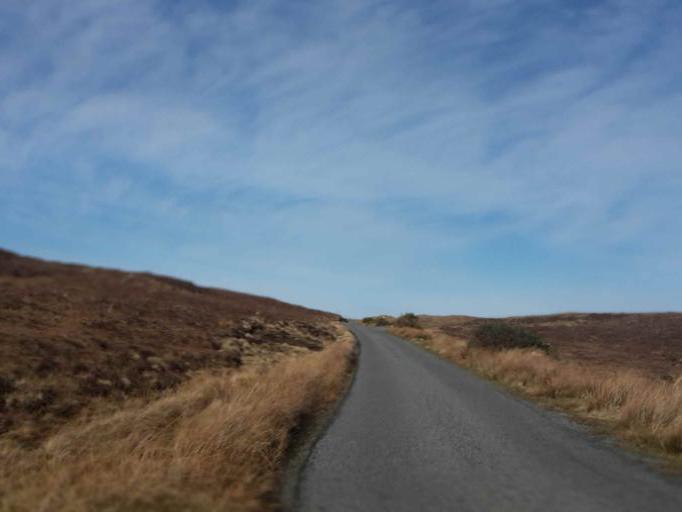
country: GB
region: Scotland
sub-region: Eilean Siar
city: Harris
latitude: 57.4439
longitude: -6.7310
